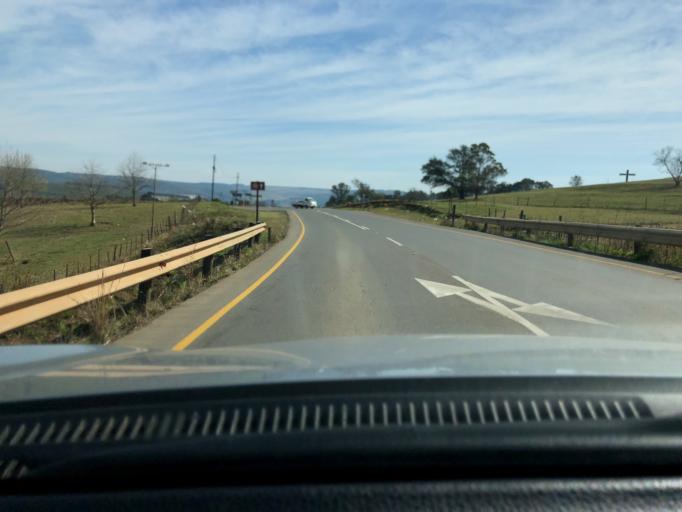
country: ZA
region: KwaZulu-Natal
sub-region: Sisonke District Municipality
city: Ixopo
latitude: -30.1678
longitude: 30.0624
